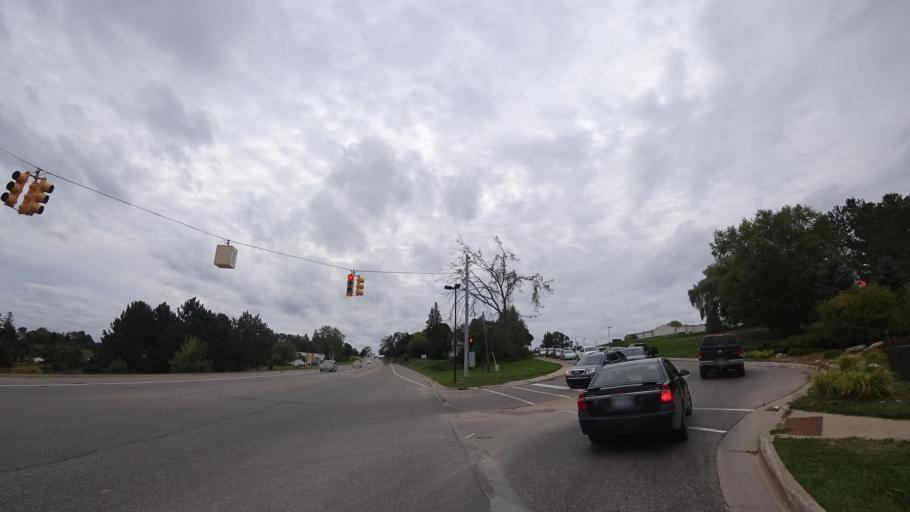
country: US
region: Michigan
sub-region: Emmet County
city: Petoskey
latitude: 45.3601
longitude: -84.9707
